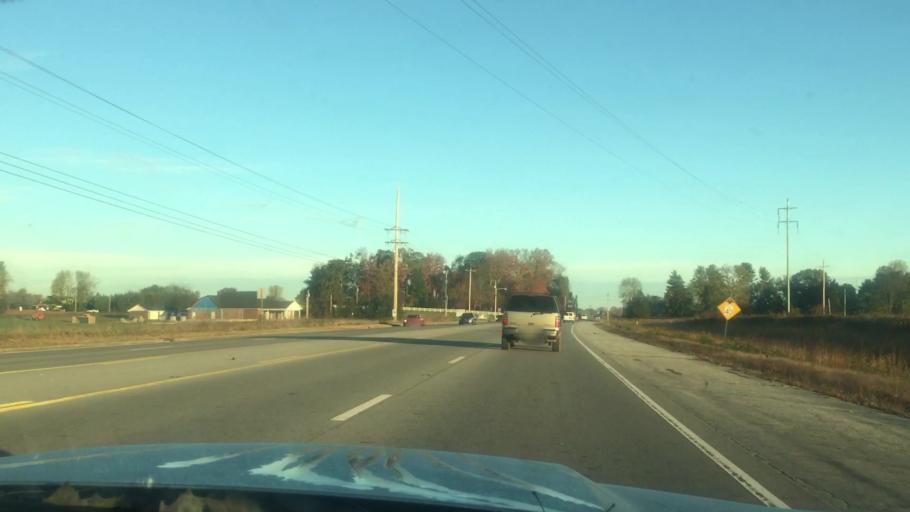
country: US
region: Tennessee
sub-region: Franklin County
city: Estill Springs
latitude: 35.2462
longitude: -86.1177
